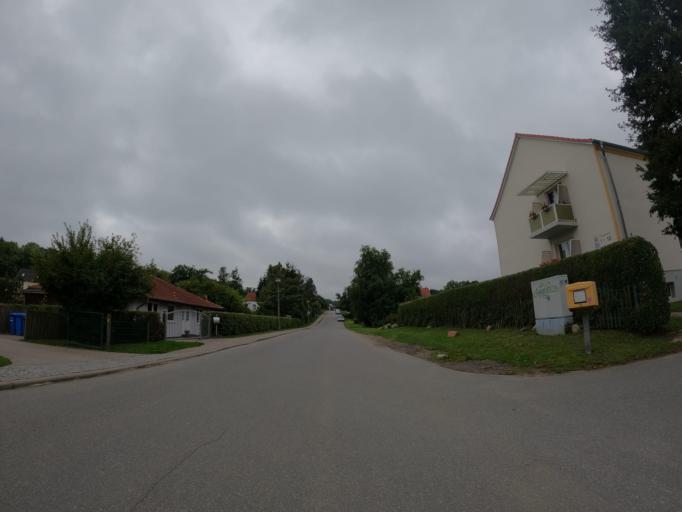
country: DE
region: Mecklenburg-Vorpommern
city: Putbus
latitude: 54.3502
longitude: 13.4823
